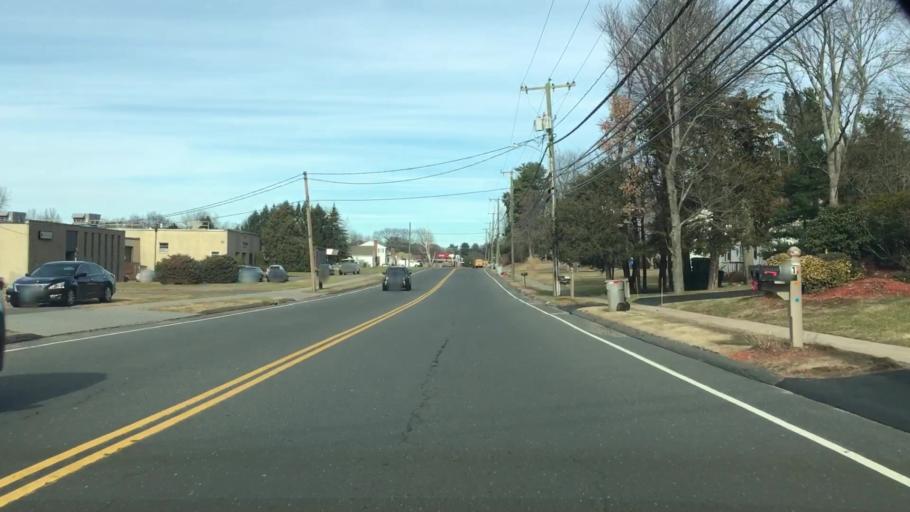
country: US
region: Connecticut
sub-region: Hartford County
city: Plainville
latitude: 41.6540
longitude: -72.9012
